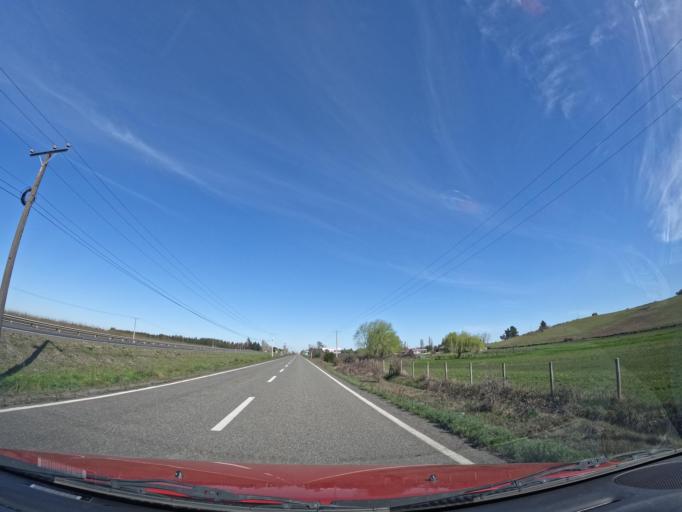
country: CL
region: Biobio
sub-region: Provincia de Biobio
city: Cabrero
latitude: -37.0132
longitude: -72.3651
